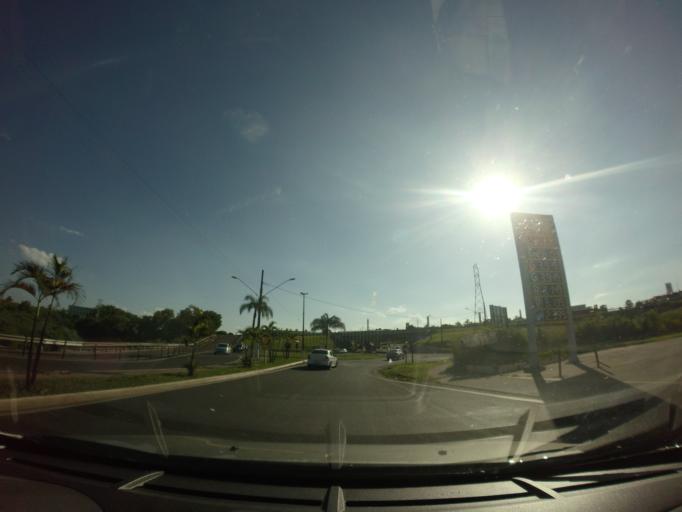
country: BR
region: Sao Paulo
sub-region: Rio Claro
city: Rio Claro
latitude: -22.4191
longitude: -47.5768
